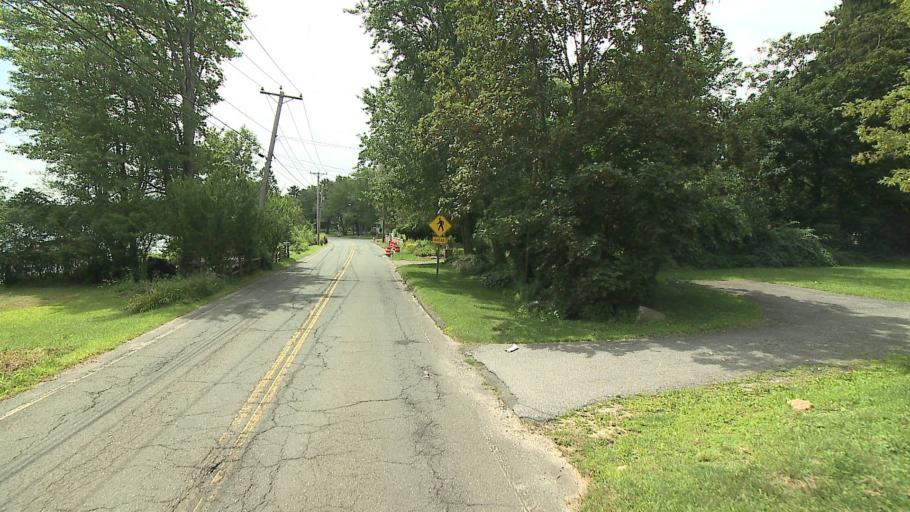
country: US
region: New York
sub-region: Putnam County
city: Putnam Lake
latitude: 41.4645
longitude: -73.5267
